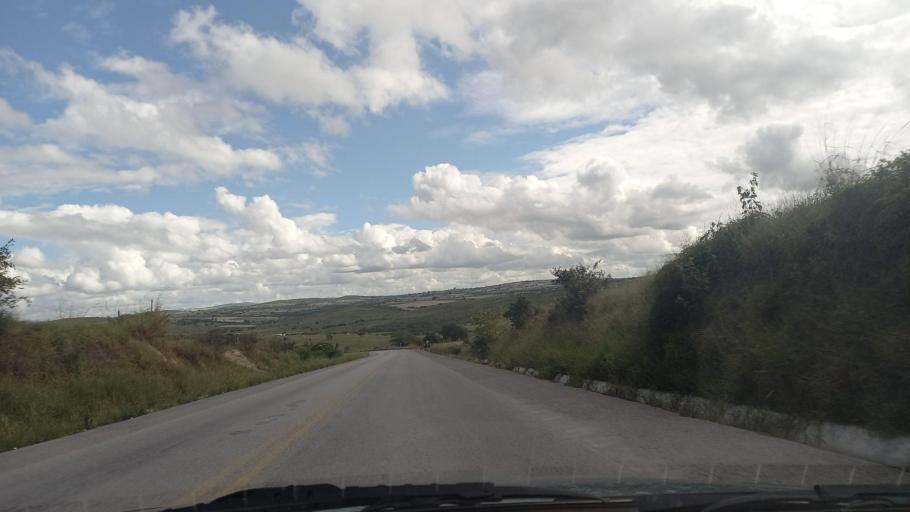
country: BR
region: Pernambuco
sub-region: Lajedo
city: Lajedo
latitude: -8.7254
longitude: -36.4299
